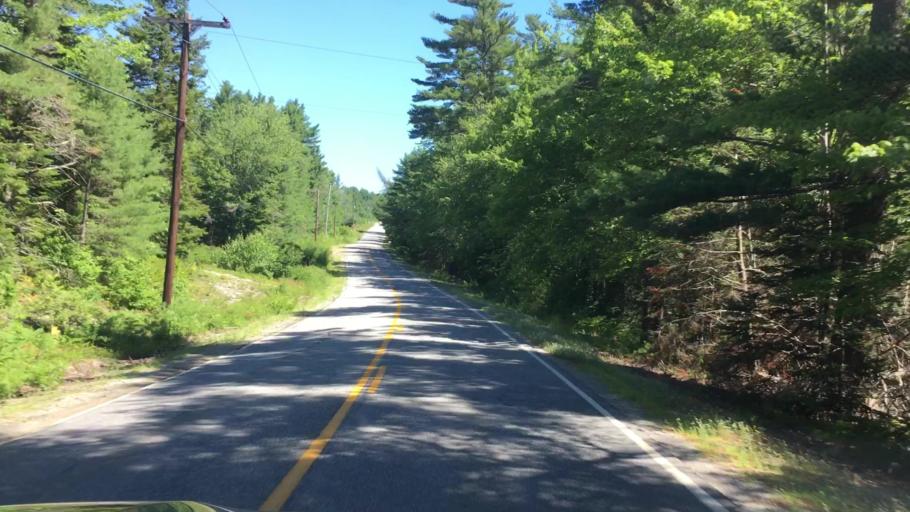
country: US
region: Maine
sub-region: Hancock County
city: Penobscot
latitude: 44.5097
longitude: -68.6744
